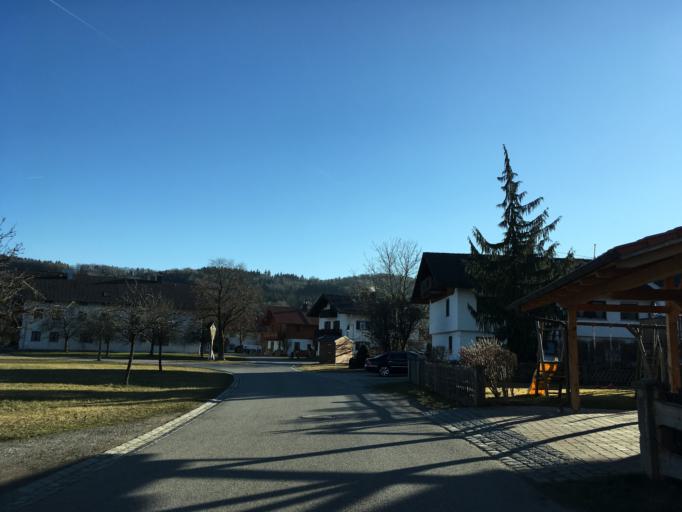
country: DE
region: Bavaria
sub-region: Upper Bavaria
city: Vagen
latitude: 47.8747
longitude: 11.8812
